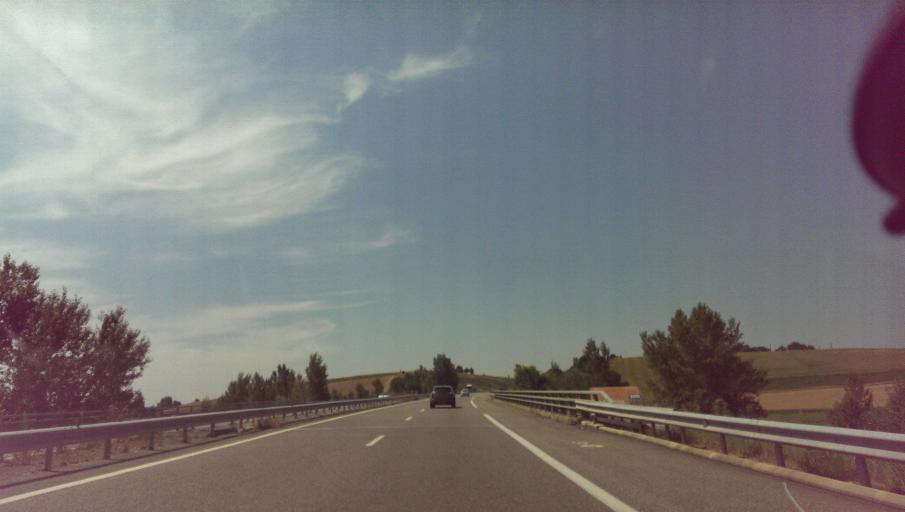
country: FR
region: Midi-Pyrenees
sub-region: Departement de la Haute-Garonne
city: Villenouvelle
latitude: 43.4107
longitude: 1.6512
